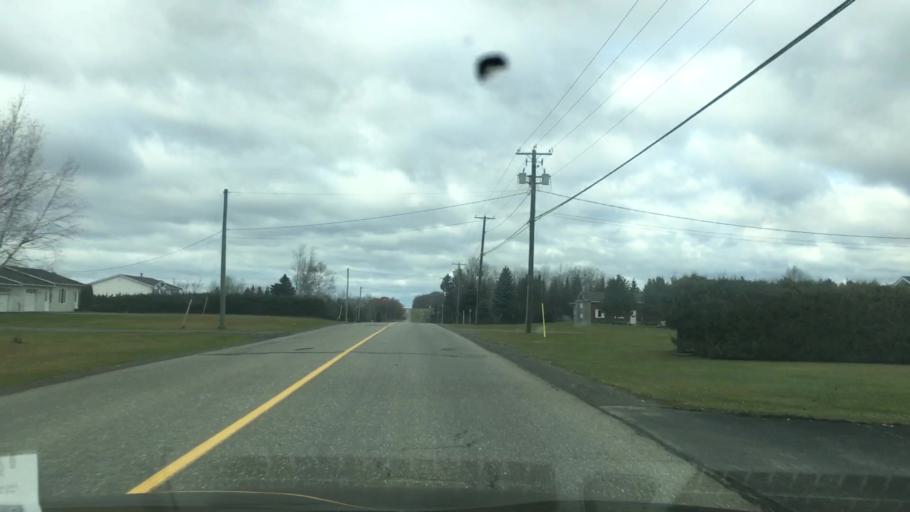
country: US
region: Maine
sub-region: Aroostook County
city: Fort Fairfield
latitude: 46.7559
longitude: -67.7639
